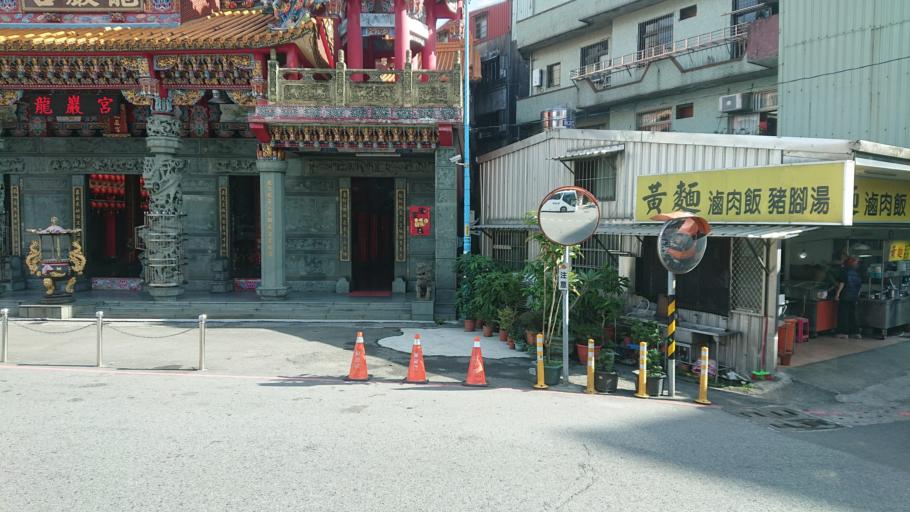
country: TW
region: Taiwan
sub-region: Keelung
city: Keelung
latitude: 25.1086
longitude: 121.8039
